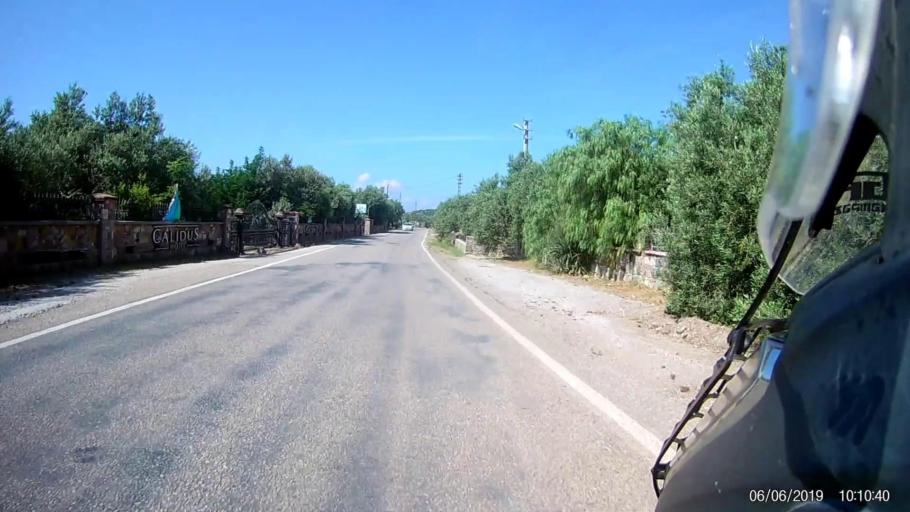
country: TR
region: Canakkale
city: Ayvacik
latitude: 39.5156
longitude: 26.4380
